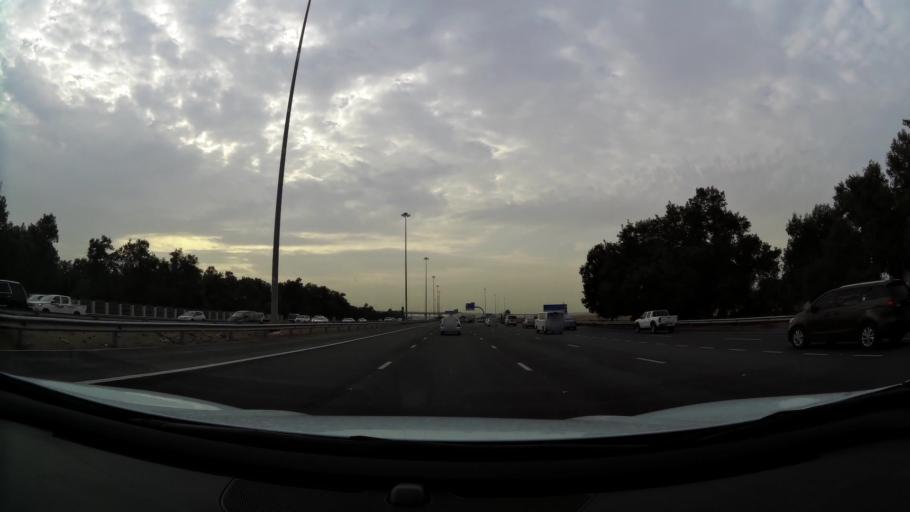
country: AE
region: Abu Dhabi
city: Abu Dhabi
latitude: 24.3184
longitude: 54.5921
